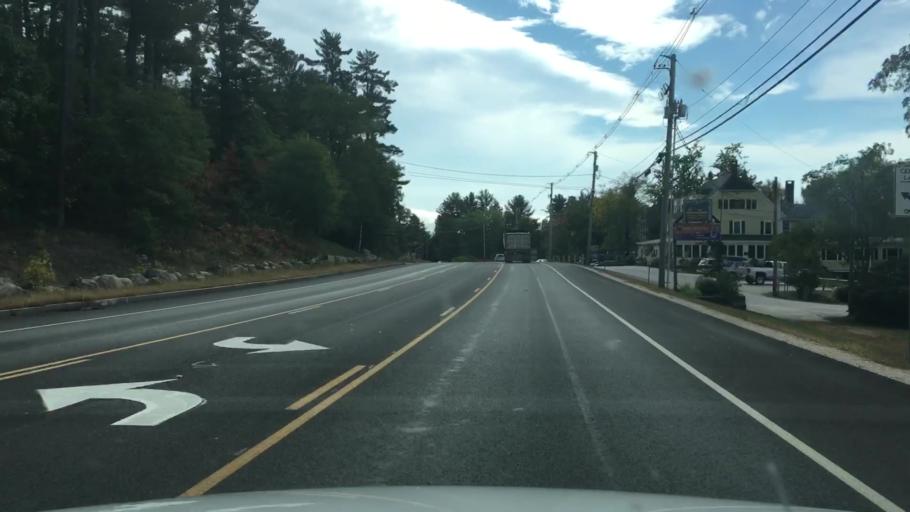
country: US
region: New Hampshire
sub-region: Carroll County
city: North Conway
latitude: 44.0693
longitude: -71.1430
